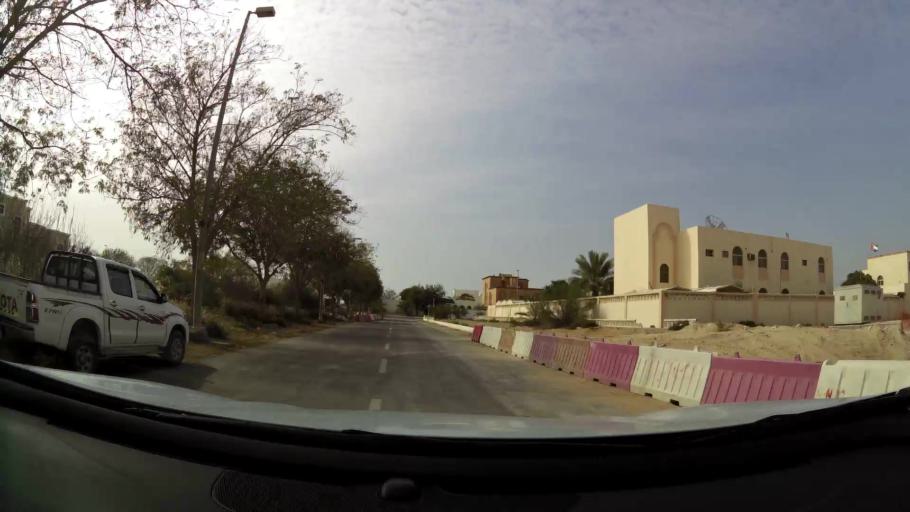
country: AE
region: Abu Dhabi
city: Abu Dhabi
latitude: 24.6015
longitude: 54.7027
